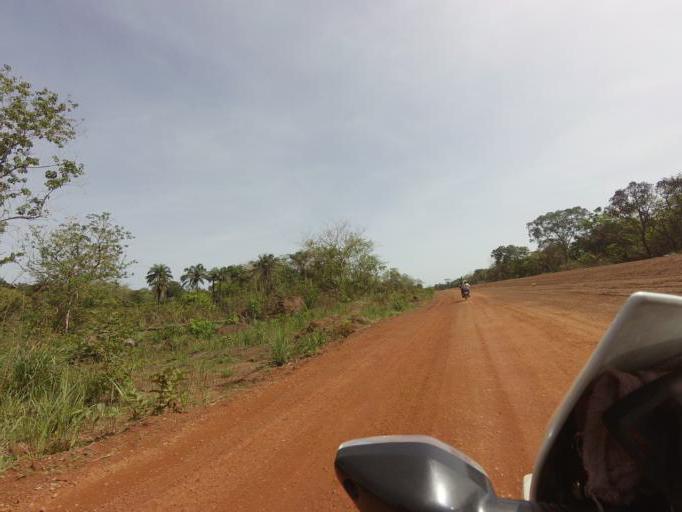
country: SL
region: Northern Province
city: Binkolo
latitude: 9.1343
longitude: -12.2187
